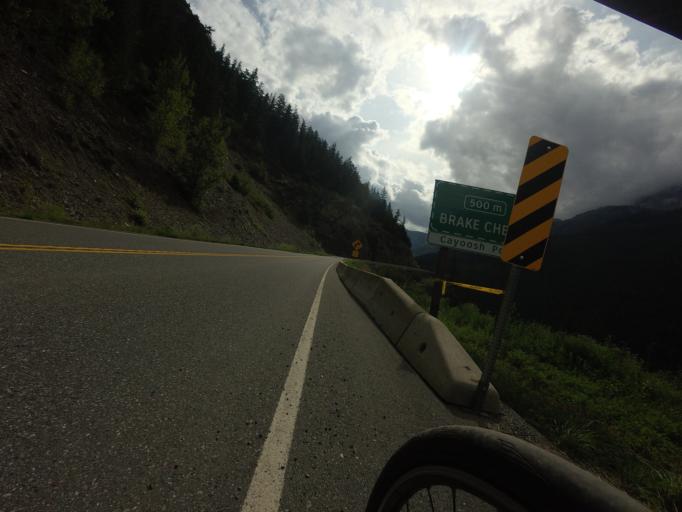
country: CA
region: British Columbia
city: Lillooet
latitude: 50.6427
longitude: -122.0330
